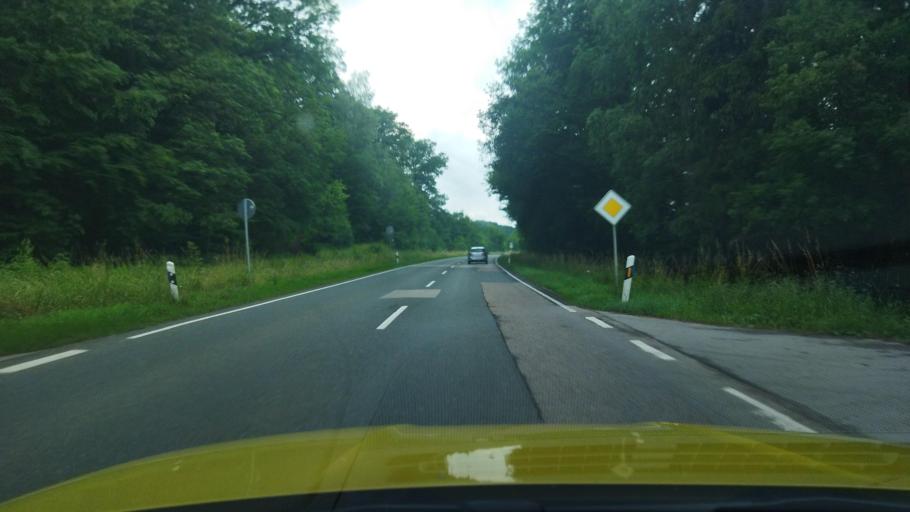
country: DE
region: Bavaria
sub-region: Regierungsbezirk Mittelfranken
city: Pfofeld
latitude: 49.1138
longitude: 10.8626
